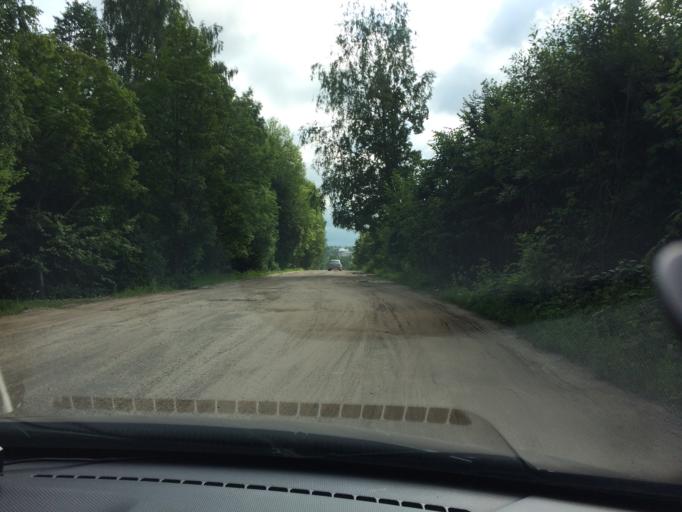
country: RU
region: Mariy-El
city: Mochalishche
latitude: 56.5458
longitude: 48.3826
